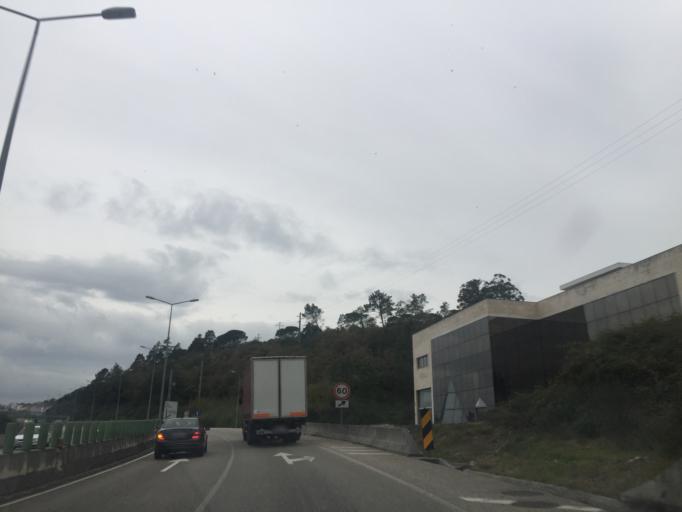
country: PT
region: Coimbra
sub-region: Coimbra
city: Coimbra
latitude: 40.1838
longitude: -8.4367
